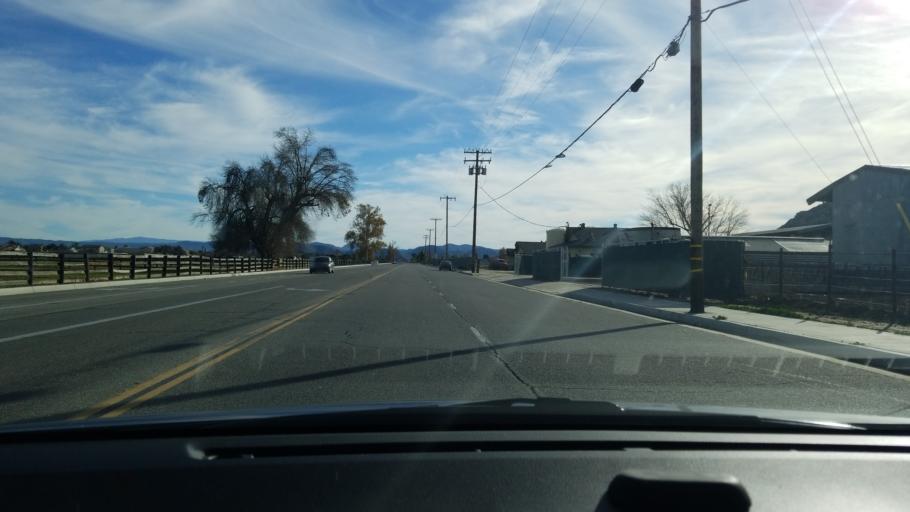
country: US
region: California
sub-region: Riverside County
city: Hemet
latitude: 33.7725
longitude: -117.0154
